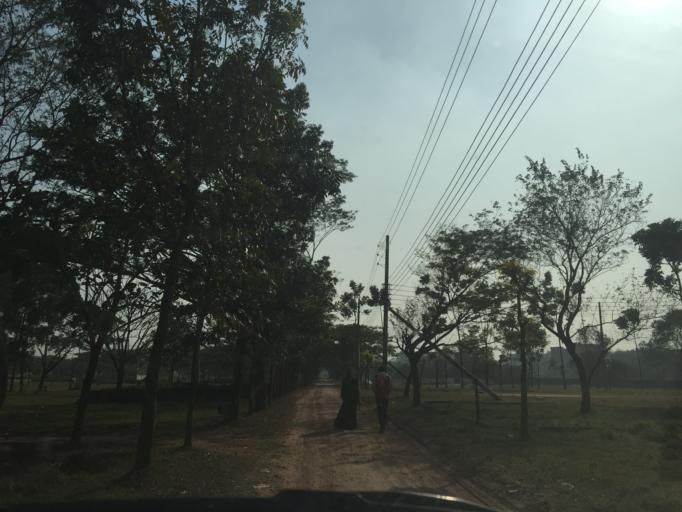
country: BD
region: Dhaka
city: Tungi
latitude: 23.8731
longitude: 90.3130
